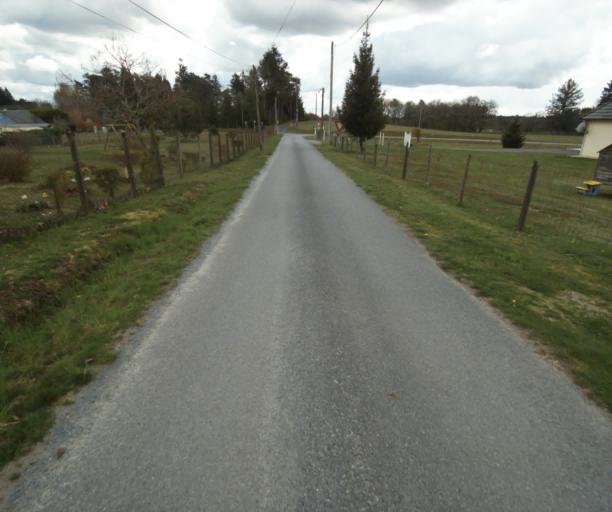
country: FR
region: Limousin
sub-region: Departement de la Correze
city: Correze
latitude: 45.2806
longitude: 1.9426
